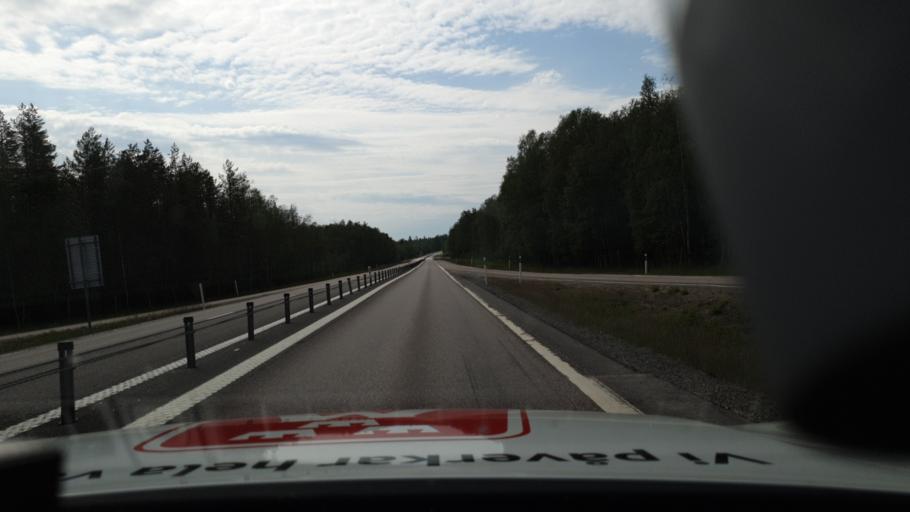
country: SE
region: Norrbotten
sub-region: Kalix Kommun
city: Toere
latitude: 65.8739
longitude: 22.4868
